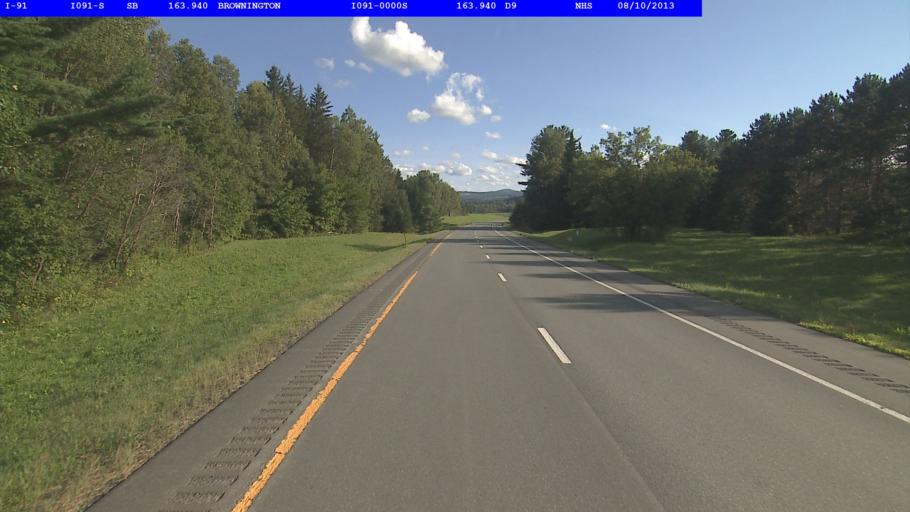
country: US
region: Vermont
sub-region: Orleans County
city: Newport
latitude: 44.8398
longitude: -72.1940
